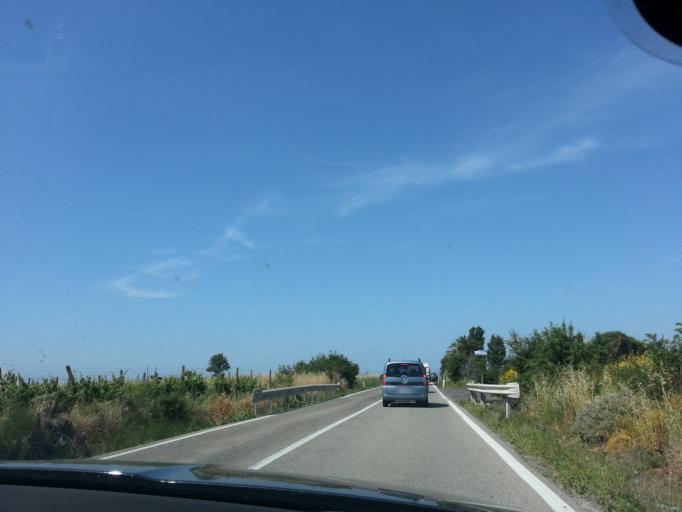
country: IT
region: Latium
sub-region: Provincia di Viterbo
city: Tarquinia
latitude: 42.2250
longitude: 11.7948
